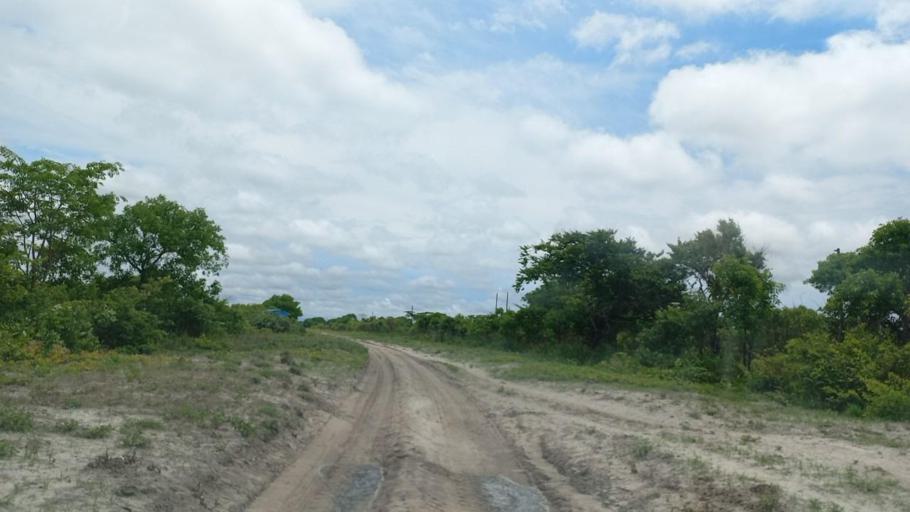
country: ZM
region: North-Western
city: Kabompo
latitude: -13.1822
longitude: 23.9502
